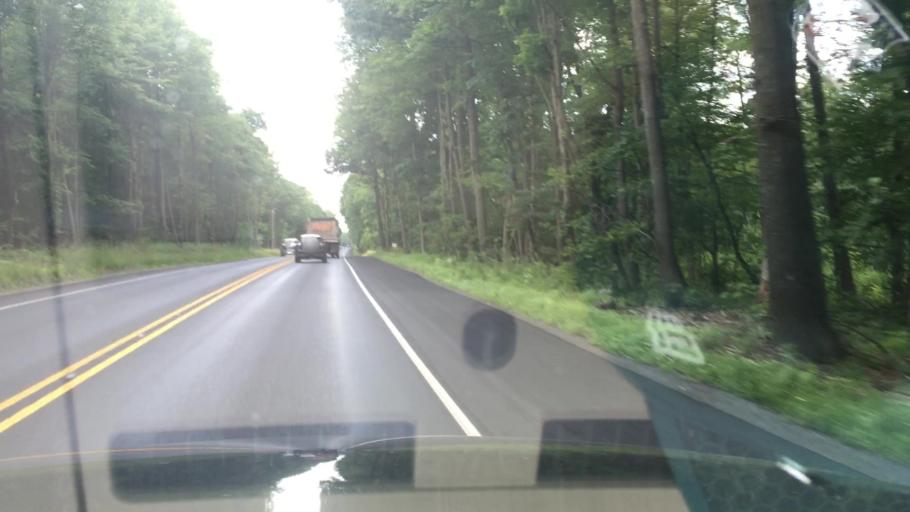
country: US
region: Pennsylvania
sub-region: Northumberland County
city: Mount Carmel
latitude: 40.7688
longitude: -76.4133
